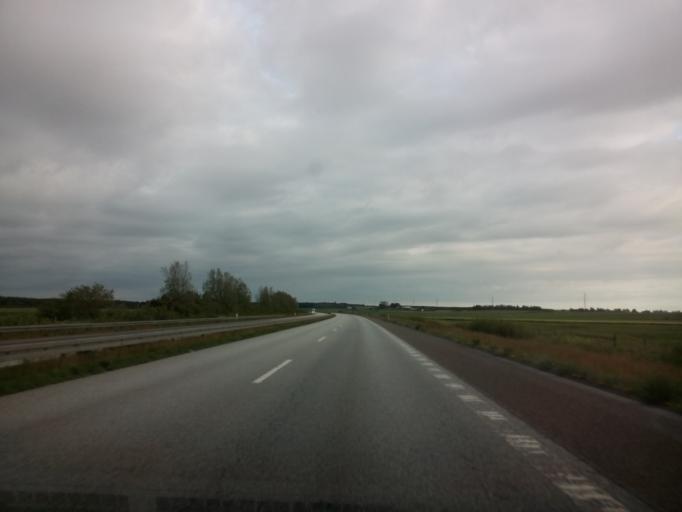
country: DK
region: North Denmark
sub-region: Hjorring Kommune
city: Vra
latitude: 57.3838
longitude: 10.0222
